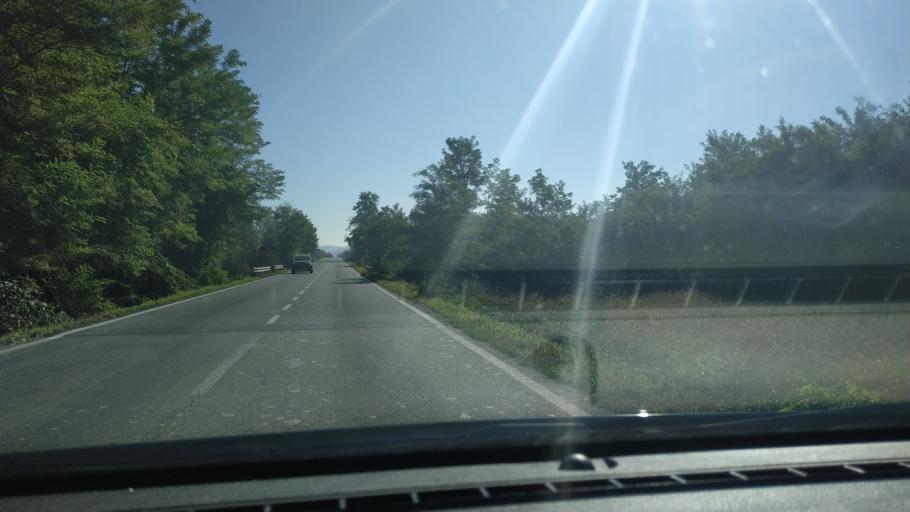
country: IT
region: Piedmont
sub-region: Provincia di Torino
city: Lauriano
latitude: 45.1628
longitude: 8.0034
